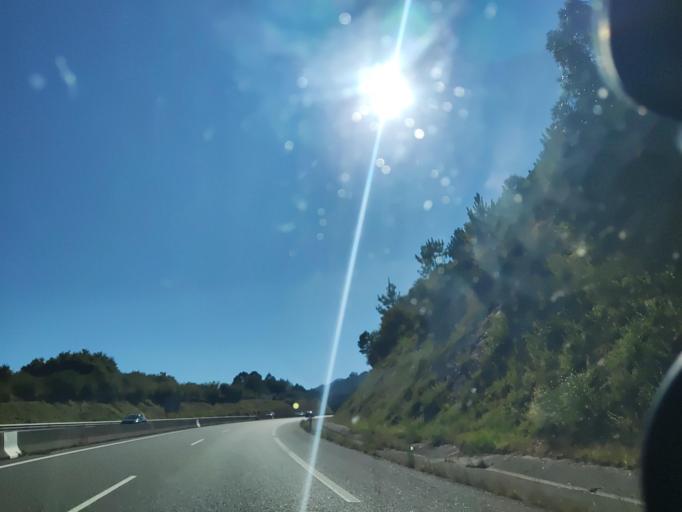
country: ES
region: Galicia
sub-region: Provincia da Coruna
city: Boiro
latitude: 42.6465
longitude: -8.9049
